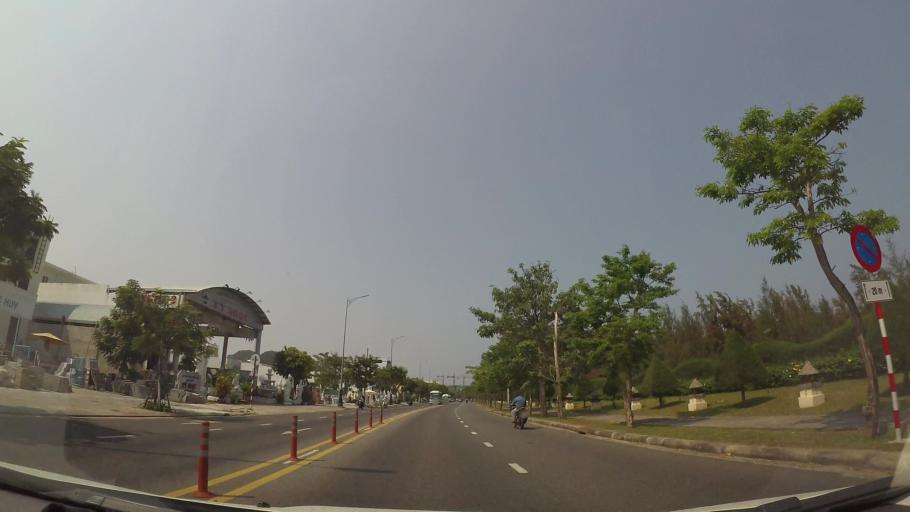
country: VN
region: Da Nang
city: Ngu Hanh Son
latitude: 15.9965
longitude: 108.2677
